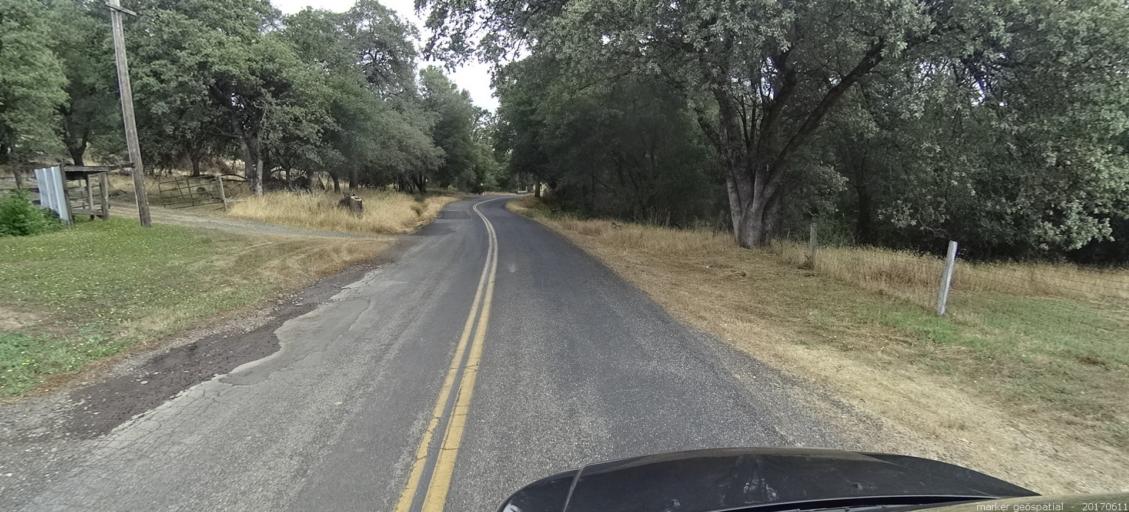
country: US
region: California
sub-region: Butte County
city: Oroville
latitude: 39.6010
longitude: -121.5354
